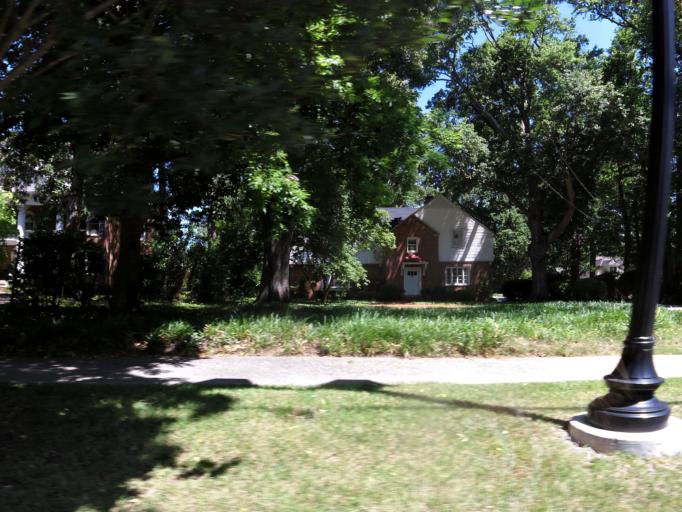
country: US
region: Georgia
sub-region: Richmond County
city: Augusta
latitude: 33.4784
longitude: -82.0244
